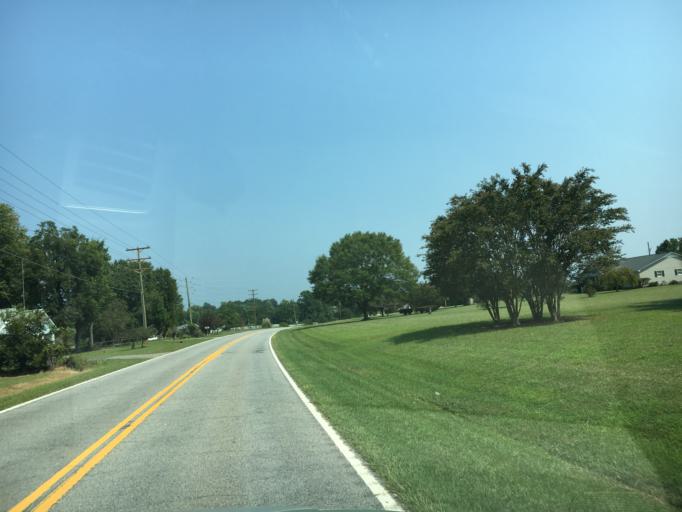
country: US
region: South Carolina
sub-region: Spartanburg County
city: Boiling Springs
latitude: 35.0682
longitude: -81.9321
